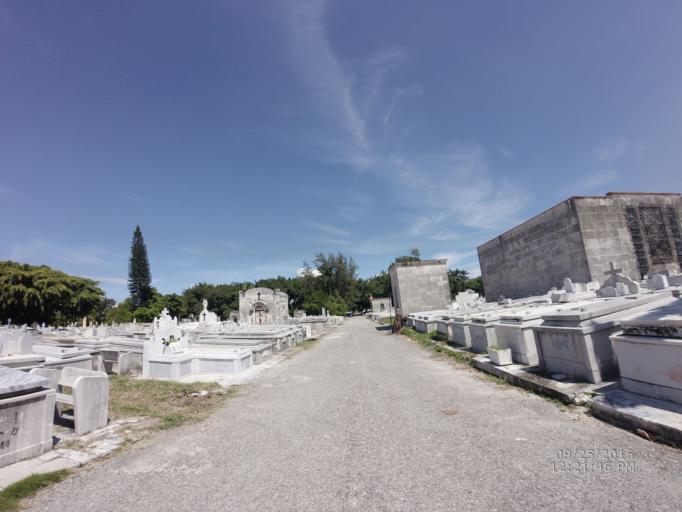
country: CU
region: La Habana
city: Havana
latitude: 23.1219
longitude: -82.3975
